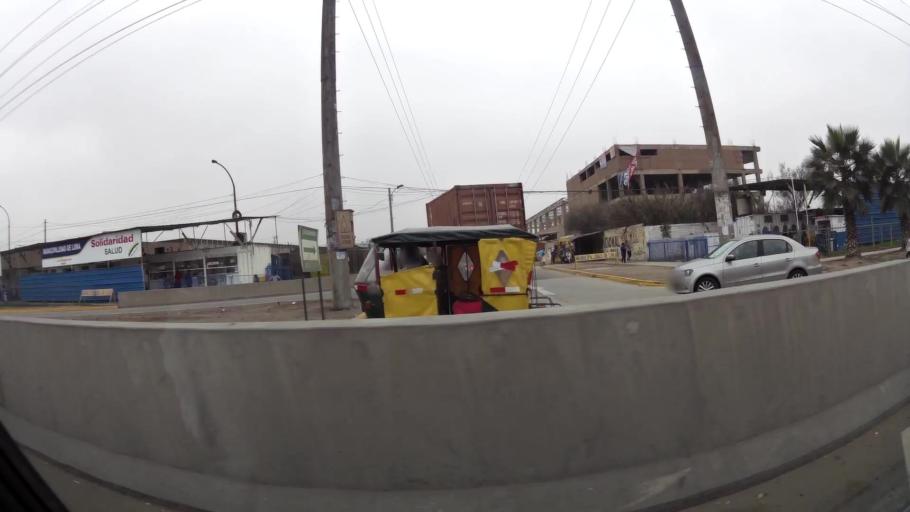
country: PE
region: Lima
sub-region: Lima
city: Carabayllo
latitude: -11.8699
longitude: -77.0709
